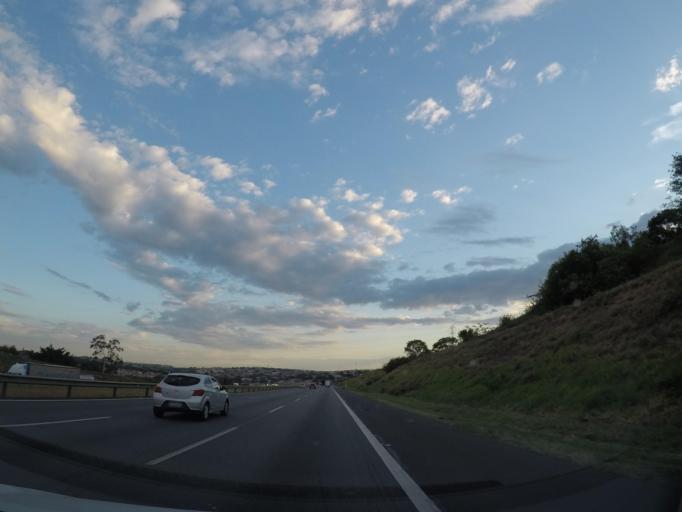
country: BR
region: Sao Paulo
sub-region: Campinas
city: Campinas
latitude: -22.9536
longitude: -47.1260
